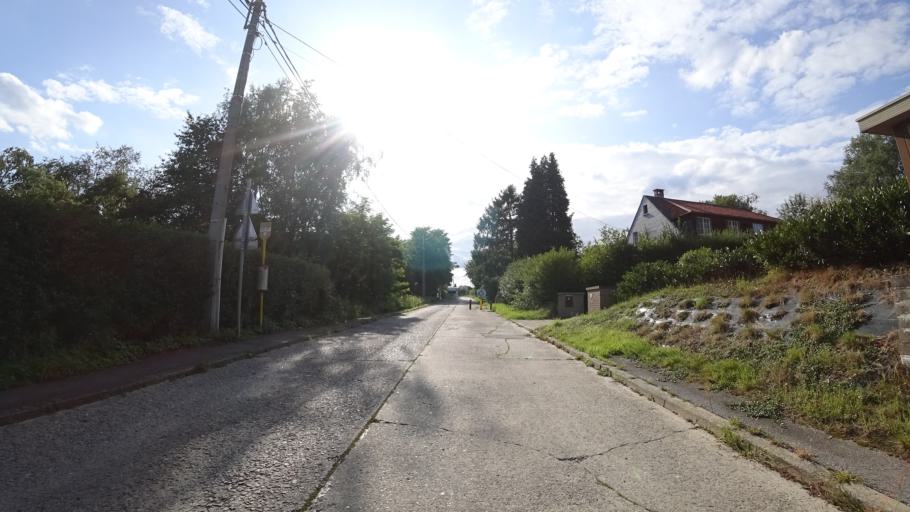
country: BE
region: Wallonia
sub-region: Province du Brabant Wallon
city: Villers-la-Ville
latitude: 50.6064
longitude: 4.5248
